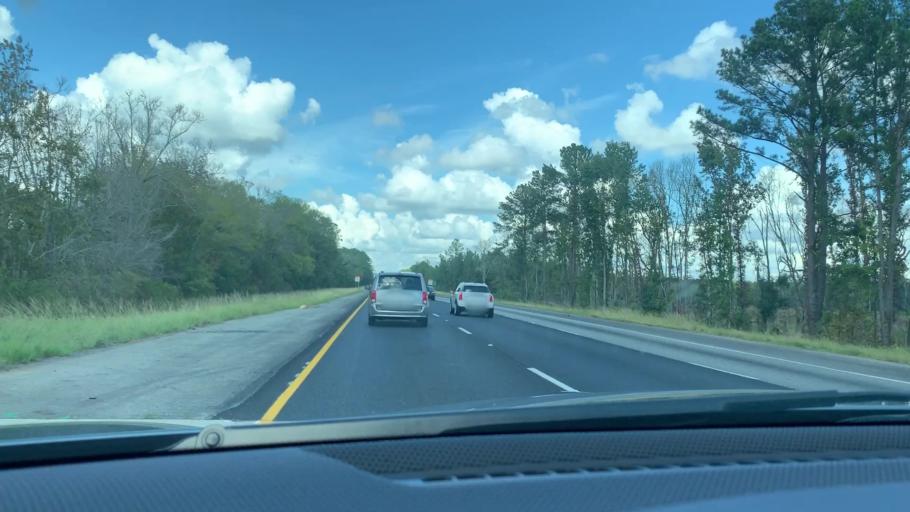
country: US
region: Georgia
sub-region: Camden County
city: Woodbine
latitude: 30.9125
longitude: -81.6859
